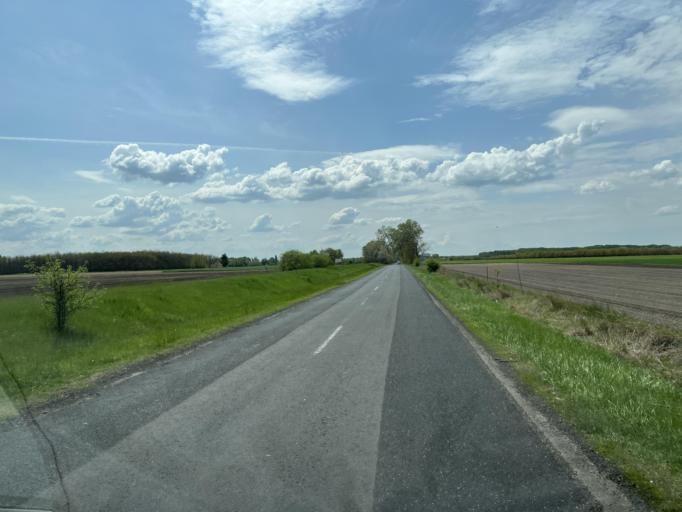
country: HU
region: Pest
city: Cegled
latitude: 47.1493
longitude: 19.7568
